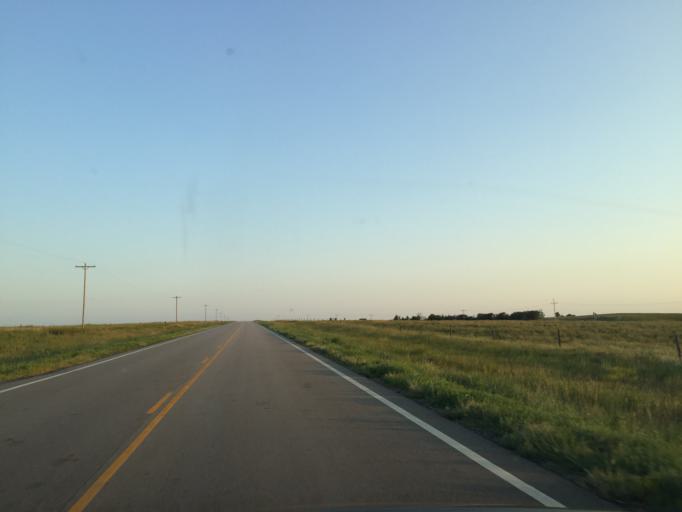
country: US
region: Kansas
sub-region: Ellsworth County
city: Ellsworth
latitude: 38.5649
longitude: -98.2017
